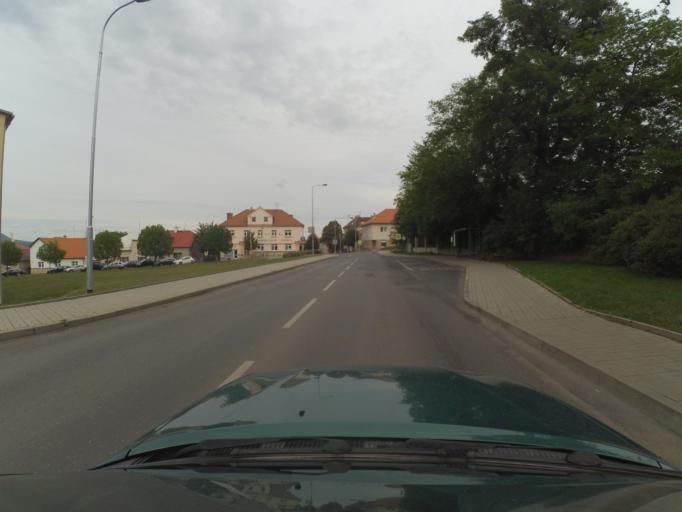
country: CZ
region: Ustecky
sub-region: Okres Louny
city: Louny
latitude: 50.3509
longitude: 13.8094
